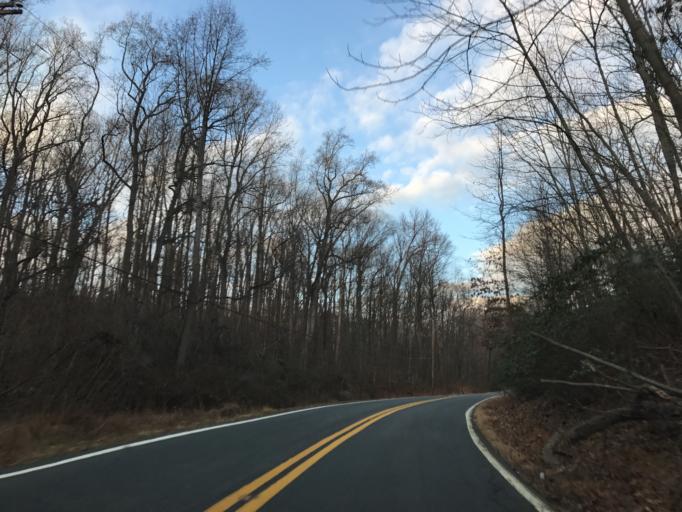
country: US
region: Maryland
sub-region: Cecil County
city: Charlestown
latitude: 39.4898
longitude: -75.9791
